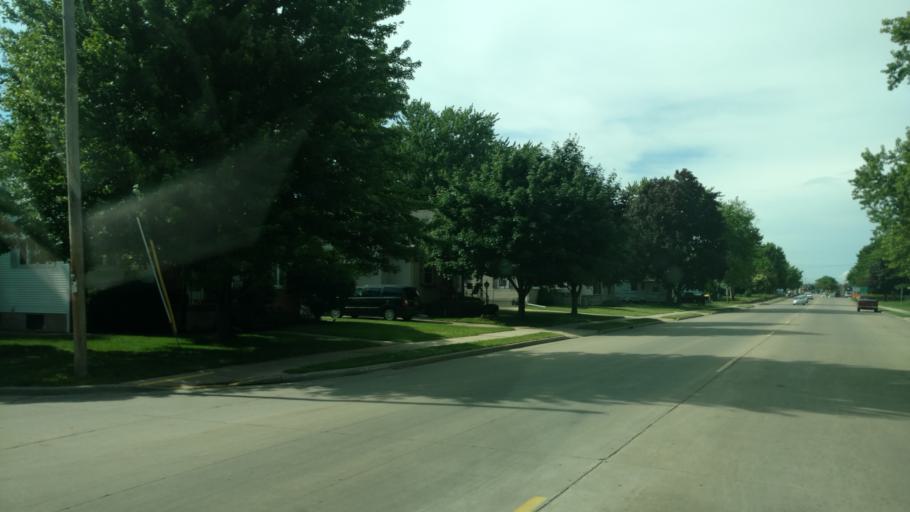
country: US
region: Wisconsin
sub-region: Monroe County
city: Tomah
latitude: 43.9687
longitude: -90.5048
